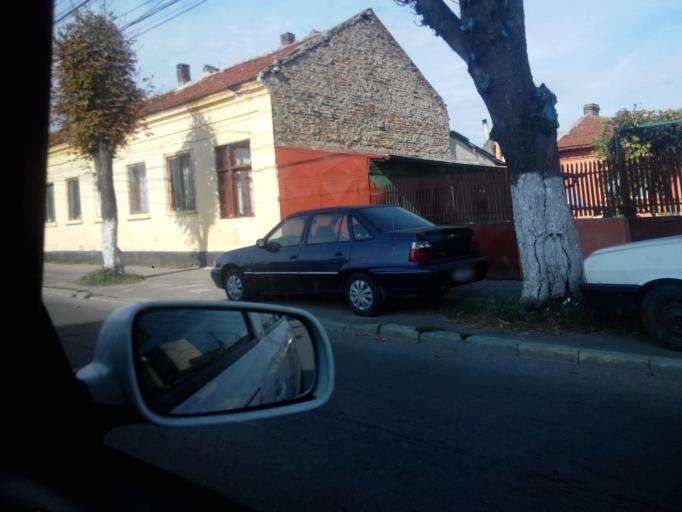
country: RO
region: Constanta
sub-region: Municipiul Constanta
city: Constanta
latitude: 44.1725
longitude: 28.6324
